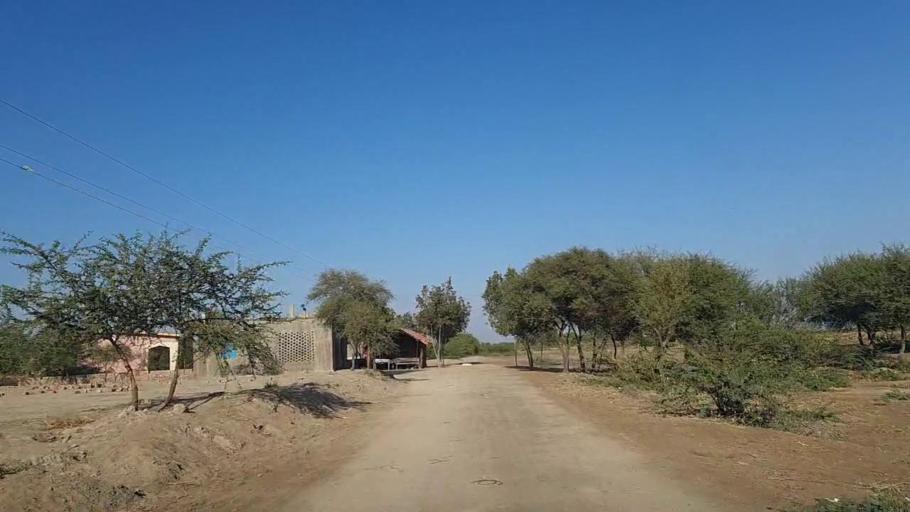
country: PK
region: Sindh
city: Naukot
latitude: 24.9690
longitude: 69.3475
